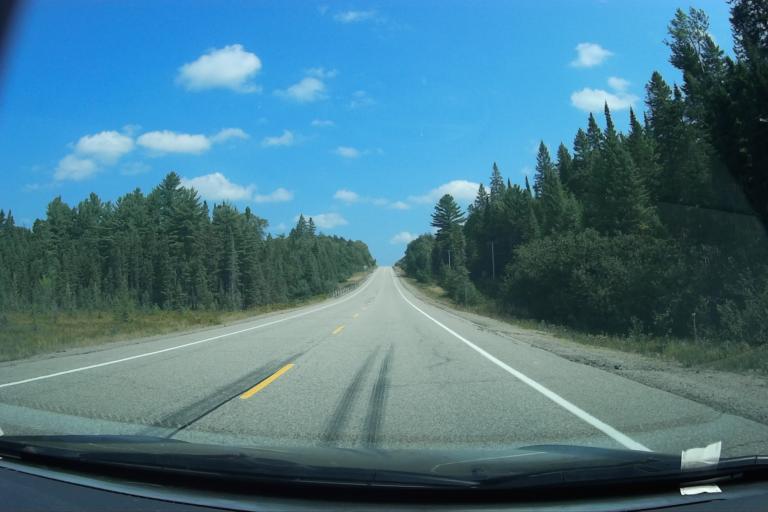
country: CA
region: Ontario
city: Huntsville
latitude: 45.5606
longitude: -78.5767
